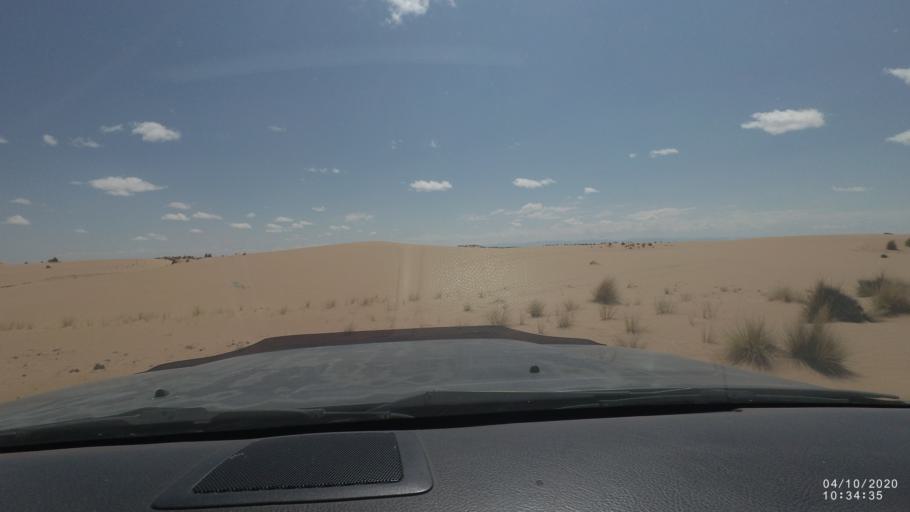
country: BO
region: Oruro
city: Poopo
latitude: -18.7048
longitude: -67.4775
